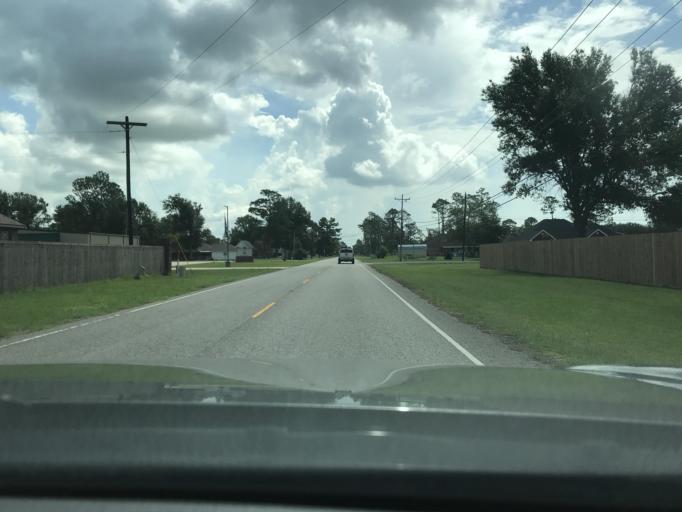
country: US
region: Louisiana
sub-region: Calcasieu Parish
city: Moss Bluff
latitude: 30.3447
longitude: -93.2257
